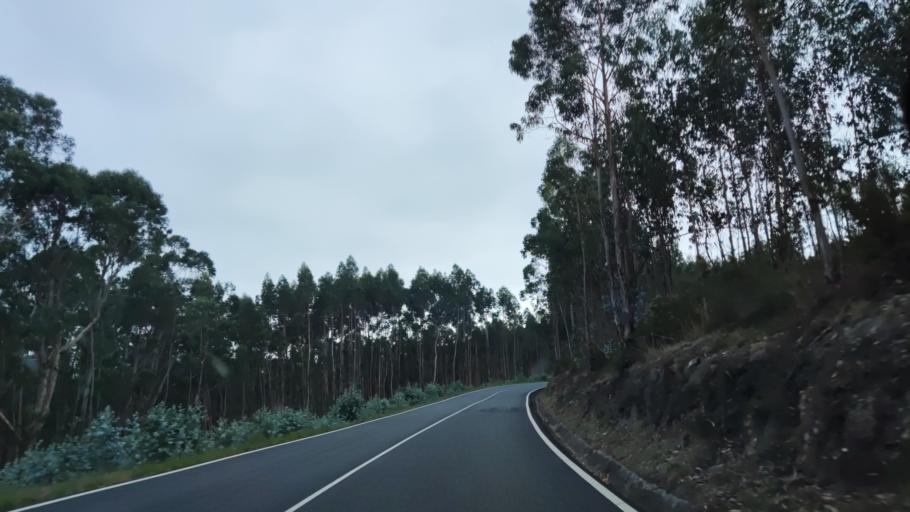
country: ES
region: Galicia
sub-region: Provincia de Pontevedra
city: Catoira
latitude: 42.6585
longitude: -8.7510
